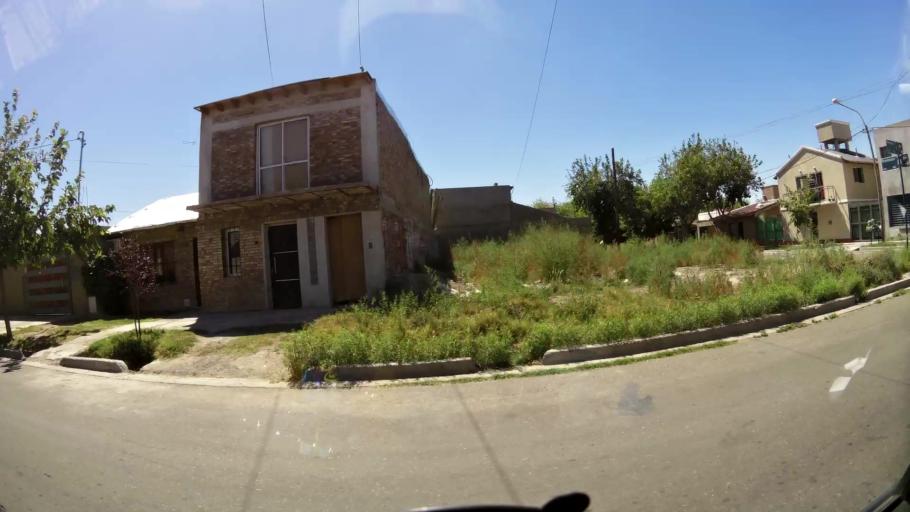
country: AR
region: Mendoza
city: Las Heras
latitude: -32.8505
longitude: -68.8481
